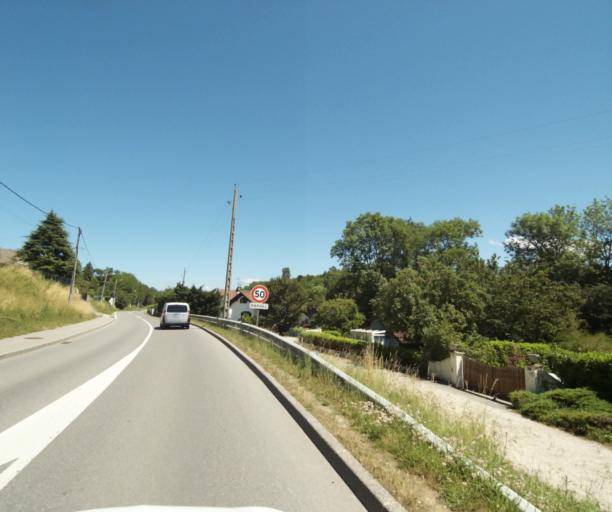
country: FR
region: Rhone-Alpes
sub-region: Departement de la Haute-Savoie
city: Veigy-Foncenex
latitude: 46.2678
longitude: 6.2721
